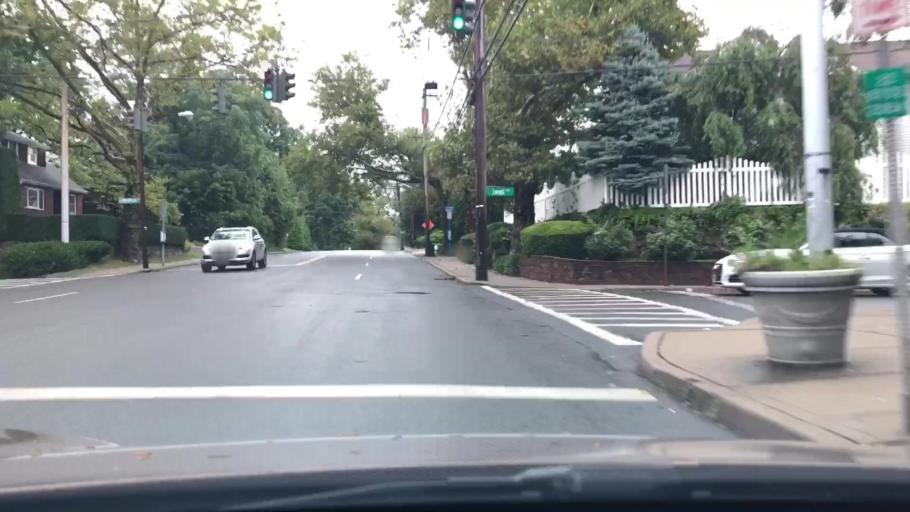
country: US
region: New York
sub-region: Westchester County
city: Greenville
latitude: 40.9767
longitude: -73.8024
